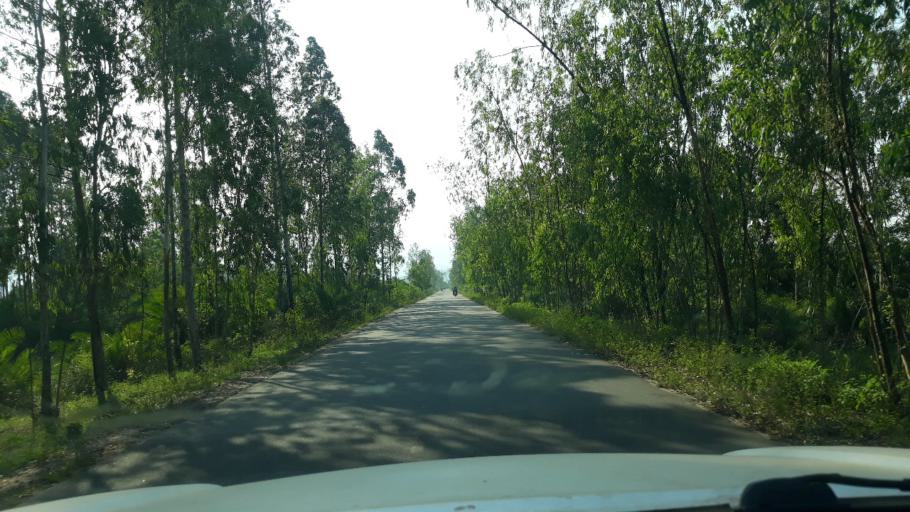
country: BI
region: Cibitoke
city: Cibitoke
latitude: -2.8151
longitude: 29.0046
